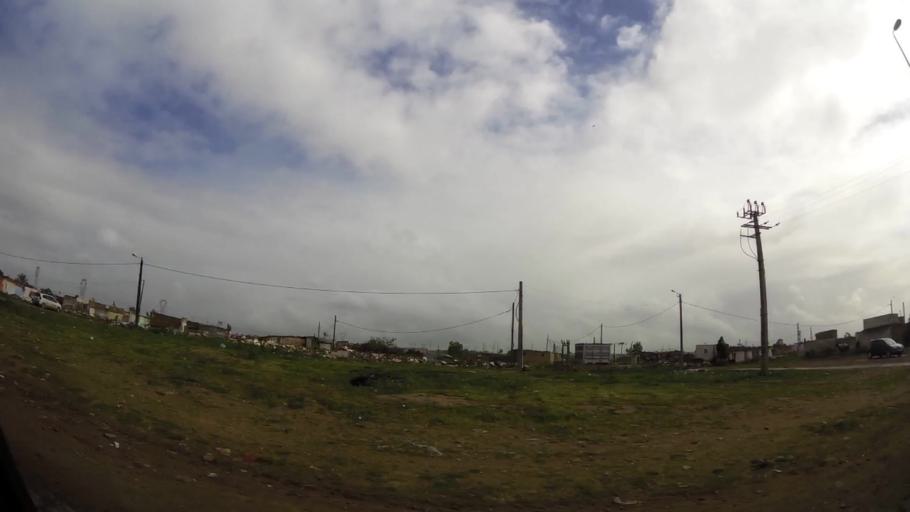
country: MA
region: Grand Casablanca
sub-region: Mohammedia
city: Mohammedia
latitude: 33.6424
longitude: -7.4271
